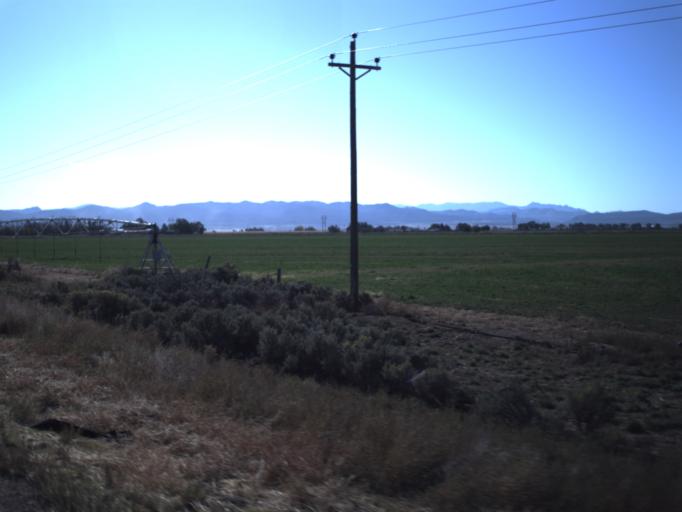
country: US
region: Utah
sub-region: Washington County
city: Enterprise
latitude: 37.7138
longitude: -113.6682
